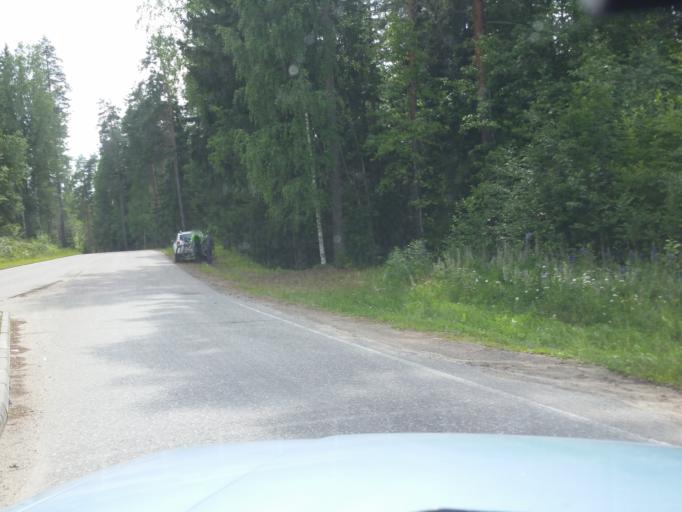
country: FI
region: Southern Savonia
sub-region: Savonlinna
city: Sulkava
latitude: 61.7995
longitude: 28.4133
